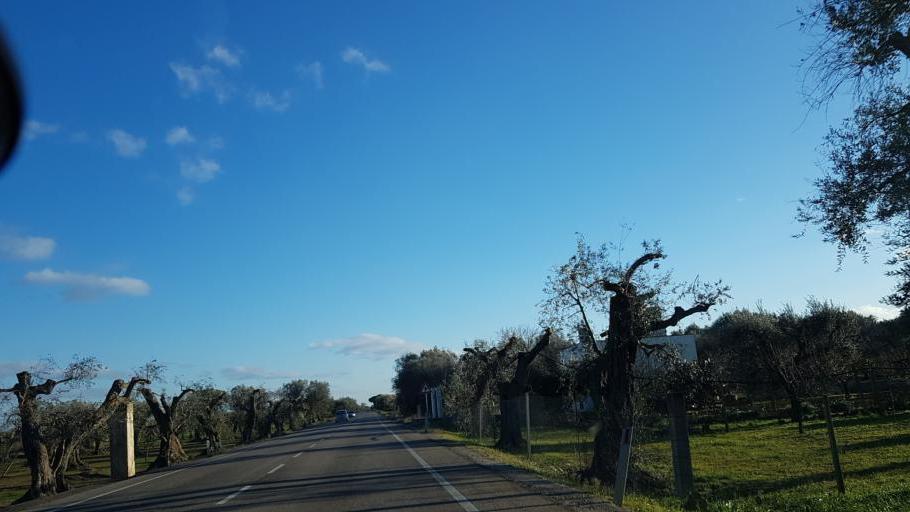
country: IT
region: Apulia
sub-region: Provincia di Lecce
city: Squinzano
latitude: 40.4571
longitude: 18.0233
